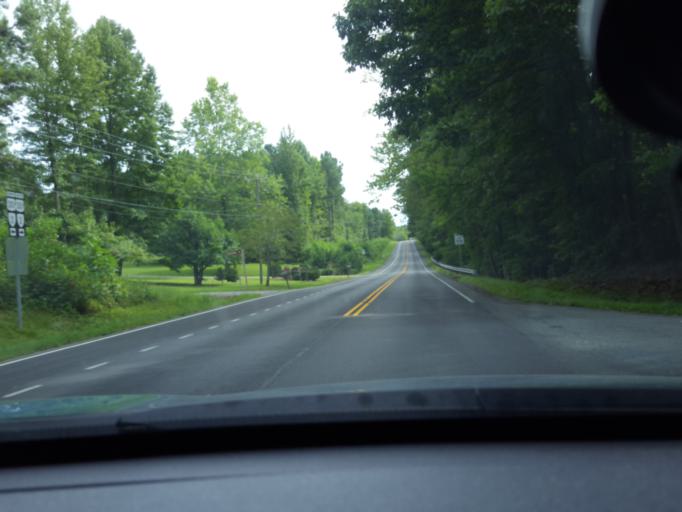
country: US
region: Virginia
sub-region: Hanover County
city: Hanover
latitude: 37.7415
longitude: -77.3586
